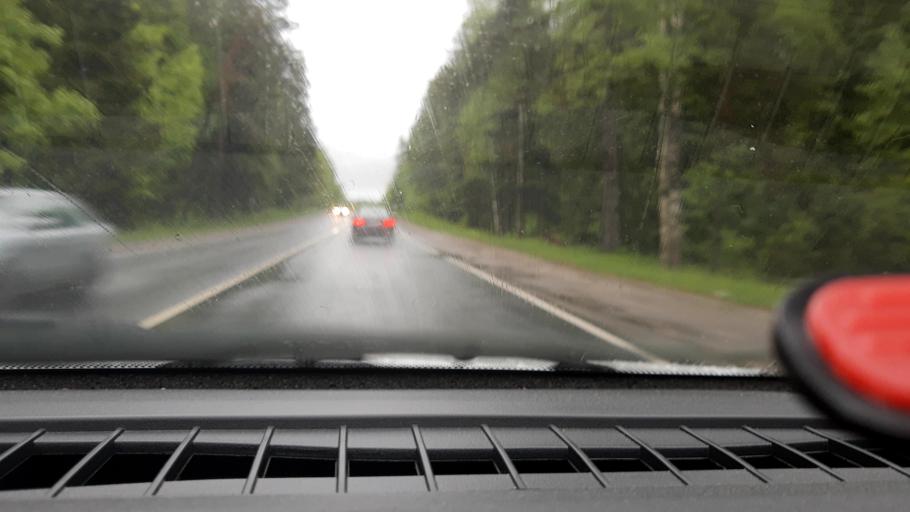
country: RU
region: Nizjnij Novgorod
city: Semenov
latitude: 56.7483
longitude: 44.3576
